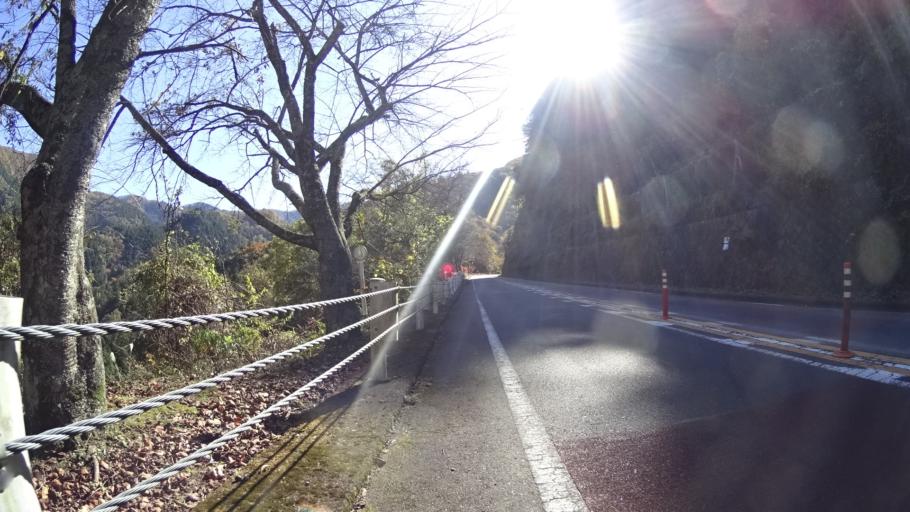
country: JP
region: Yamanashi
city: Uenohara
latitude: 35.7637
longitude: 139.0214
